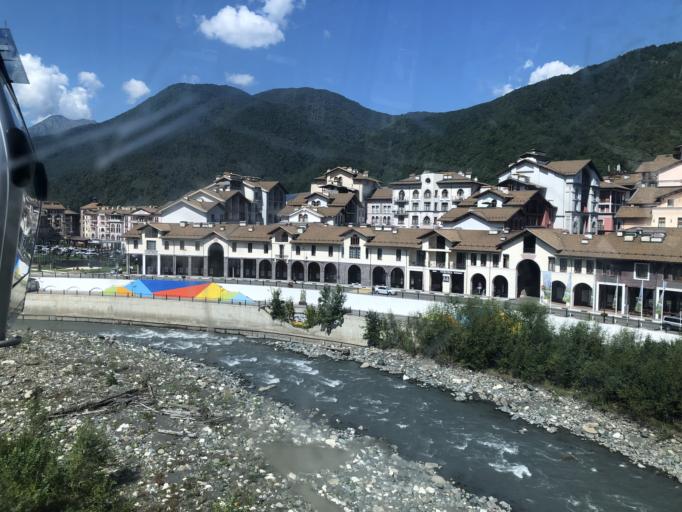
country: RU
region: Krasnodarskiy
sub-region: Sochi City
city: Krasnaya Polyana
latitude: 43.6820
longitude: 40.2662
